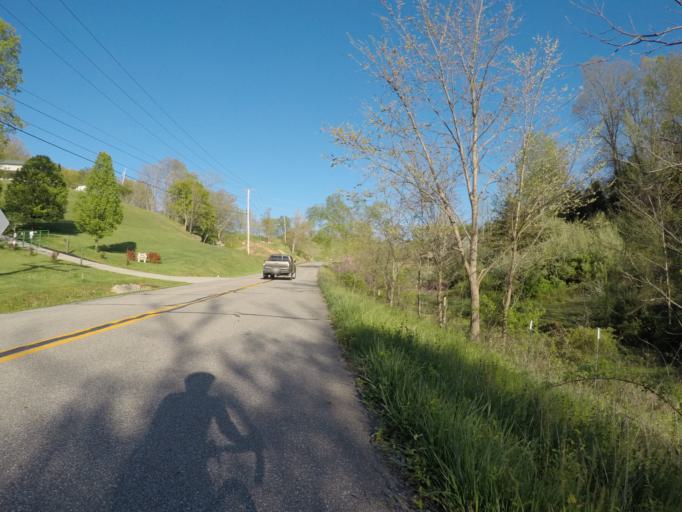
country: US
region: Kentucky
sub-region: Boyd County
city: Catlettsburg
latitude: 38.3707
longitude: -82.6572
